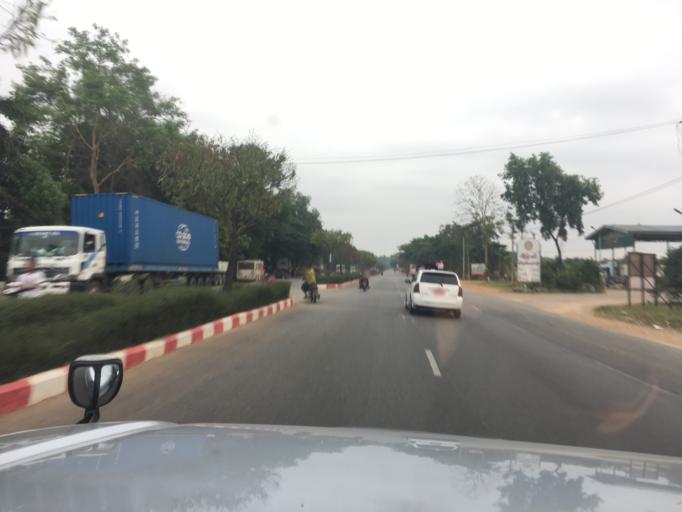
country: MM
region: Bago
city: Thanatpin
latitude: 17.1861
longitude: 96.3872
